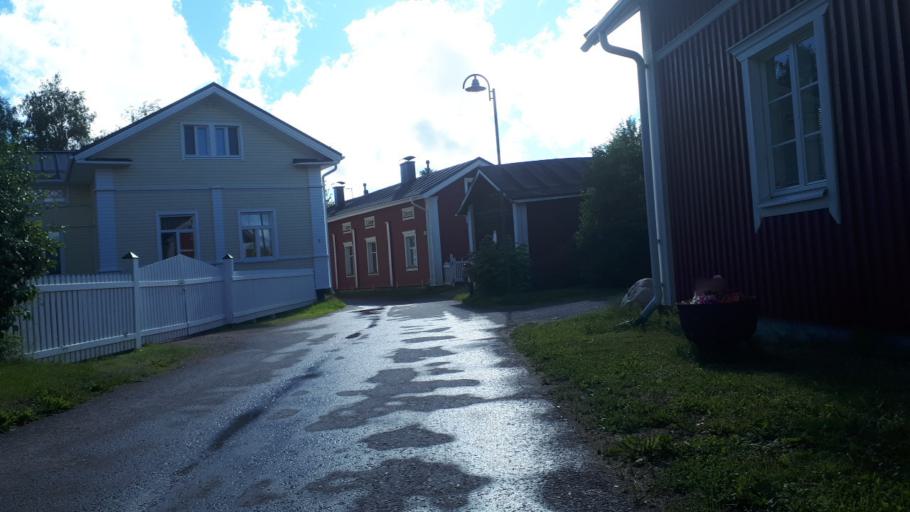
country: FI
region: Northern Ostrobothnia
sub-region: Oulunkaari
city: Ii
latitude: 65.3262
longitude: 25.3731
